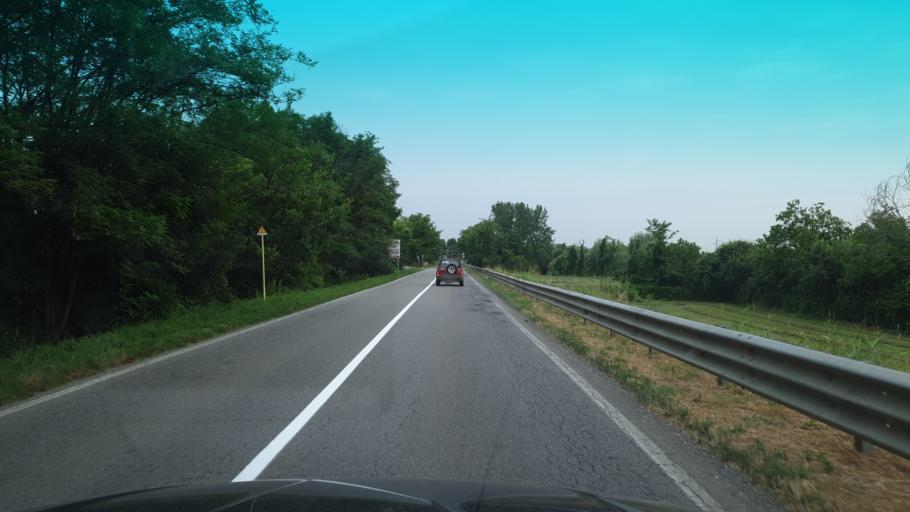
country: IT
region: Lombardy
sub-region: Provincia di Bergamo
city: Badalasco
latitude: 45.5320
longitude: 9.5380
